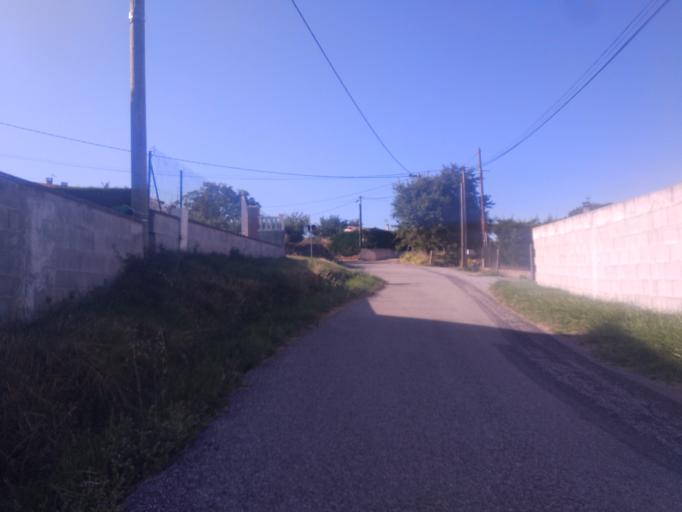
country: FR
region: Rhone-Alpes
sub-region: Departement de l'Ardeche
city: Vernosc-les-Annonay
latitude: 45.1863
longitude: 4.7396
